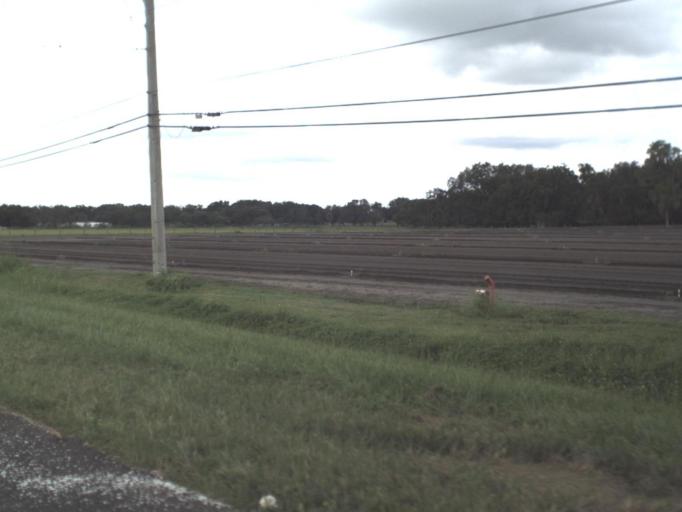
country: US
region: Florida
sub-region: Hillsborough County
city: Plant City
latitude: 27.9463
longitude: -82.1213
